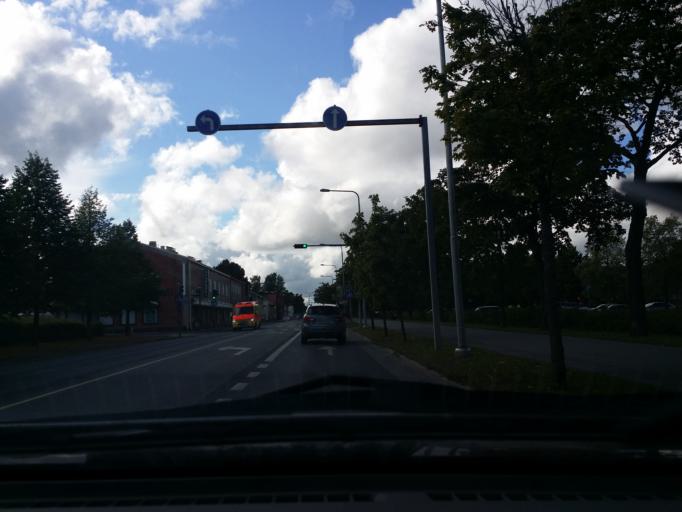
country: FI
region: Satakunta
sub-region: Pori
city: Pori
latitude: 61.4853
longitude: 21.7709
